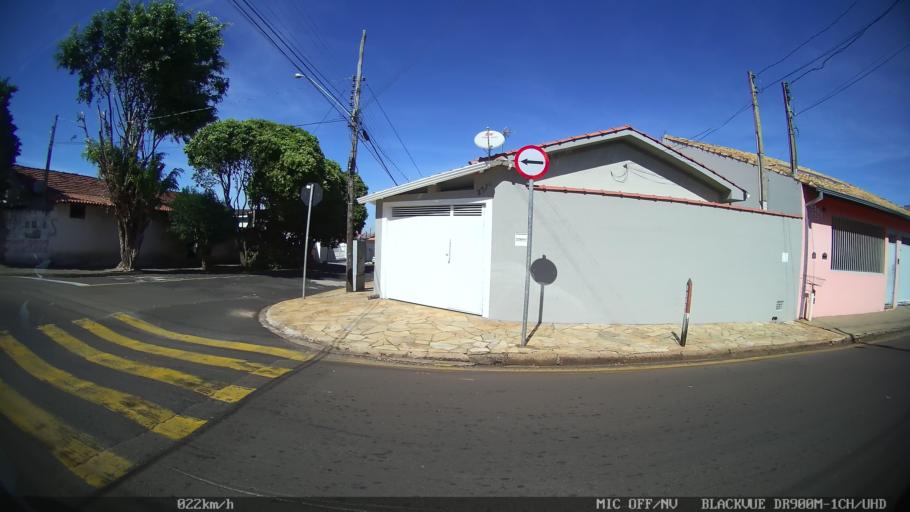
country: BR
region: Sao Paulo
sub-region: Franca
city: Franca
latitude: -20.5470
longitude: -47.3862
